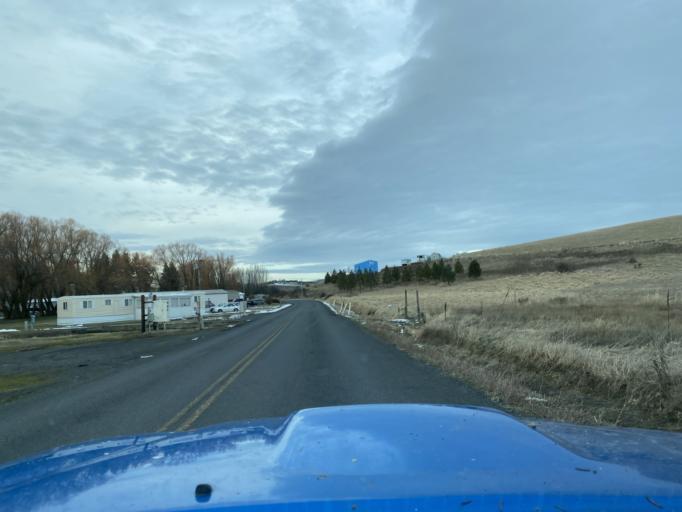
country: US
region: Idaho
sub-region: Latah County
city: Moscow
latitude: 46.7095
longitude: -116.9501
